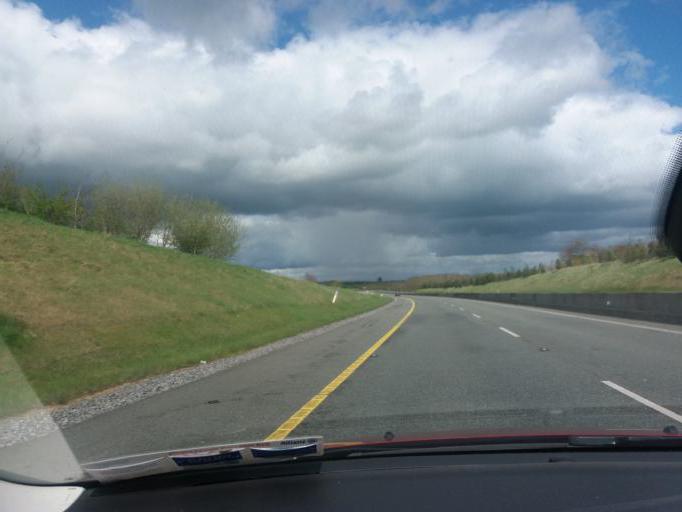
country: IE
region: Leinster
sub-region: Laois
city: Rathdowney
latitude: 52.8149
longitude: -7.4935
